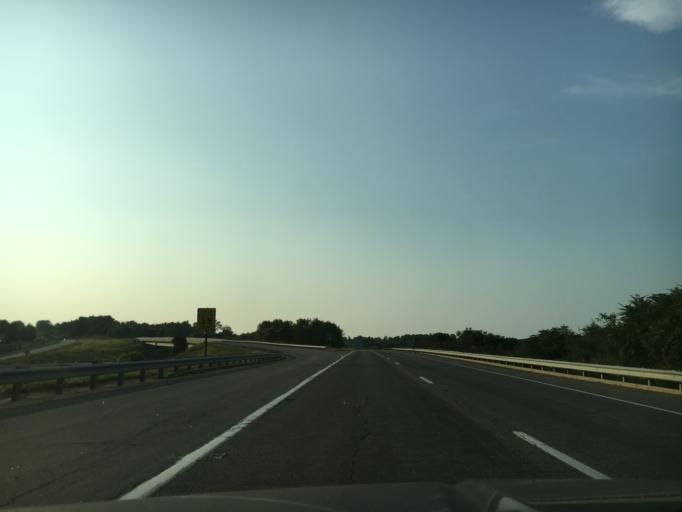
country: US
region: Virginia
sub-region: Appomattox County
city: Appomattox
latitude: 37.3465
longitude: -78.8059
